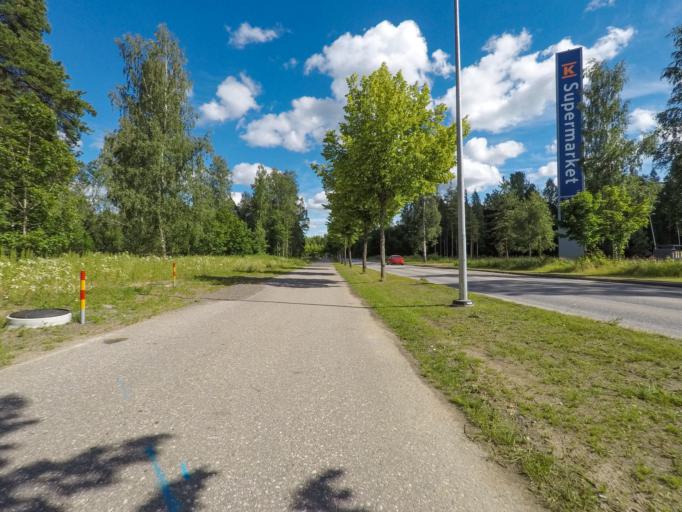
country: FI
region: South Karelia
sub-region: Lappeenranta
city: Lappeenranta
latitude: 61.0618
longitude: 28.2366
